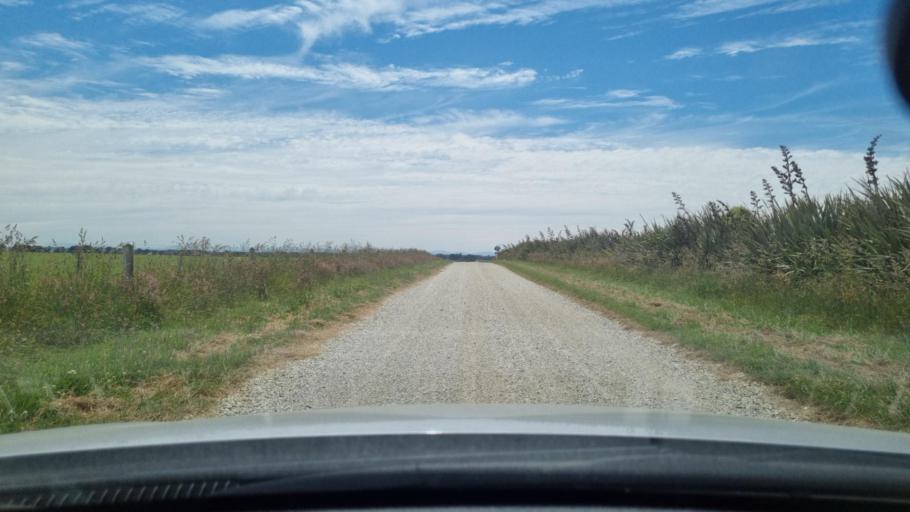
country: NZ
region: Southland
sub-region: Invercargill City
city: Invercargill
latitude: -46.4004
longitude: 168.2616
